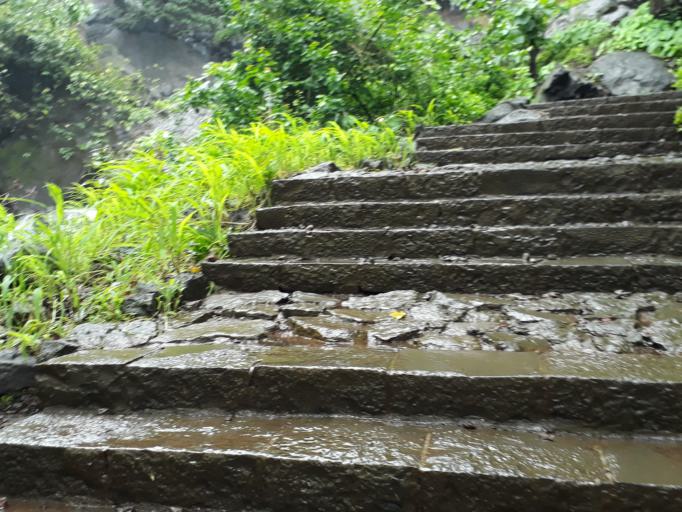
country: IN
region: Maharashtra
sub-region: Raigarh
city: Khopoli
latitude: 18.8394
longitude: 73.3841
